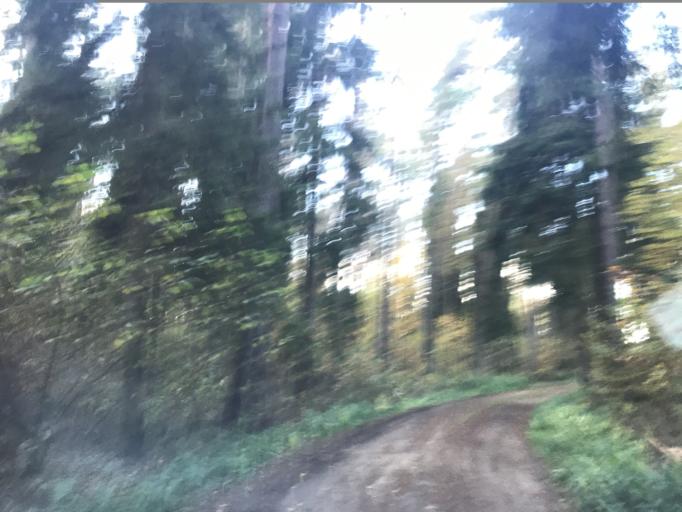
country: PL
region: Warmian-Masurian Voivodeship
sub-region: Powiat dzialdowski
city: Lidzbark
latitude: 53.2301
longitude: 19.7934
